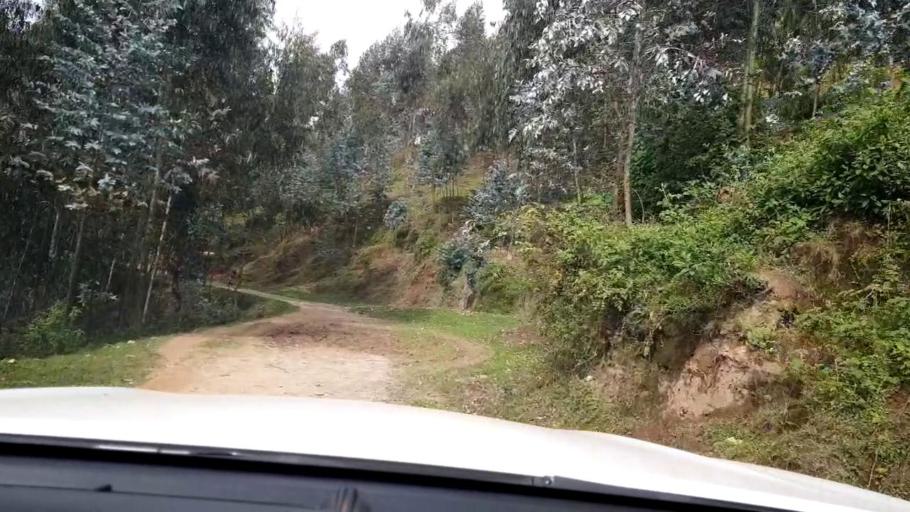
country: RW
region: Western Province
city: Kibuye
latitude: -1.8882
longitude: 29.4518
